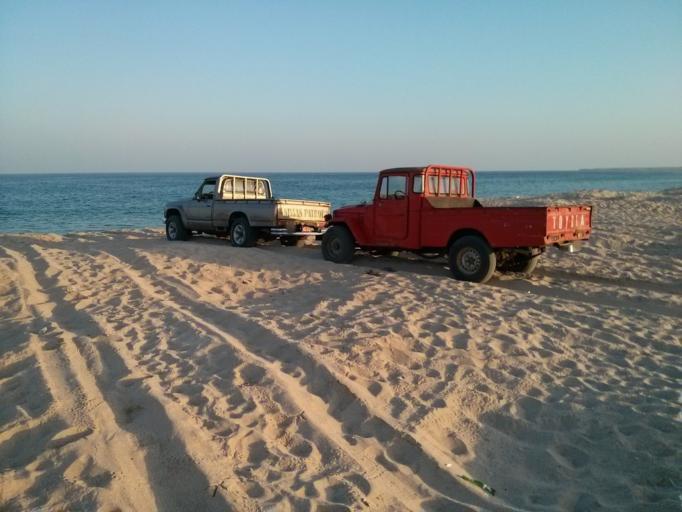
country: OM
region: Ash Sharqiyah
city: Sur
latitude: 22.5277
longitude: 59.7981
